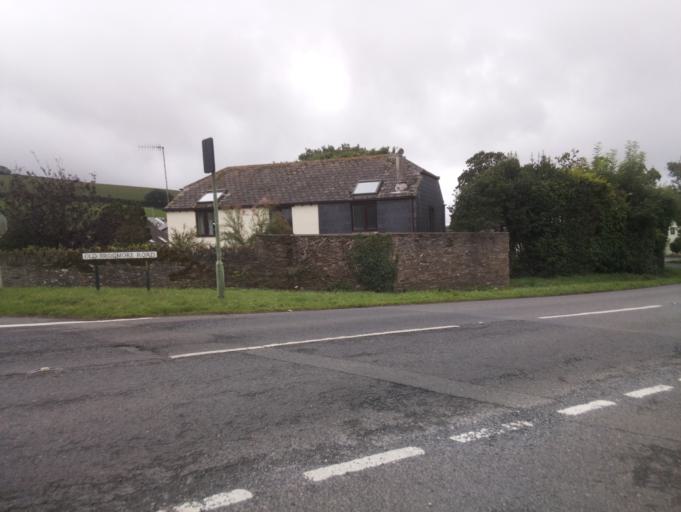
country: GB
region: England
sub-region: Devon
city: Kingsbridge
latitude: 50.2714
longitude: -3.7183
